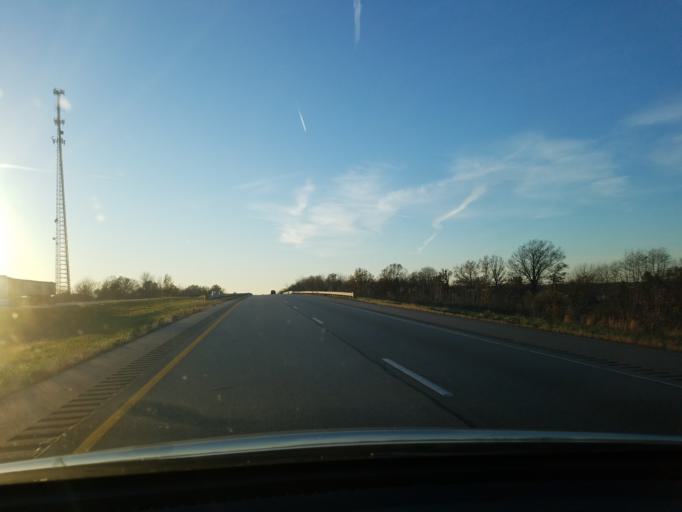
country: US
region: Indiana
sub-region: Gibson County
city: Haubstadt
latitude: 38.1698
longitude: -87.4372
